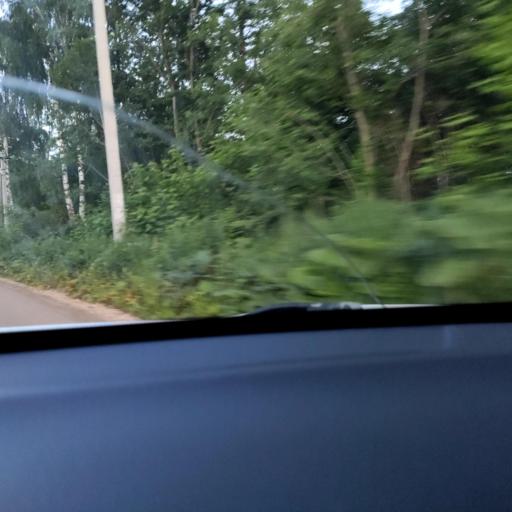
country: RU
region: Tatarstan
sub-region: Gorod Kazan'
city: Kazan
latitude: 55.8479
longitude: 49.1661
